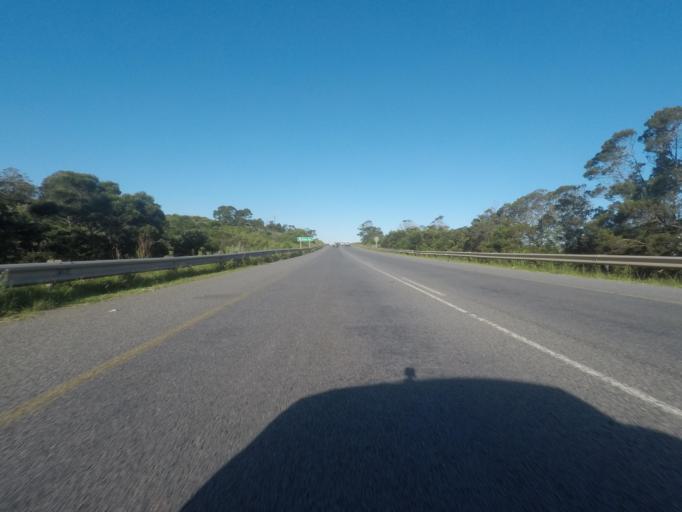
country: ZA
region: Eastern Cape
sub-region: Buffalo City Metropolitan Municipality
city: East London
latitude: -33.0503
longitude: 27.8142
